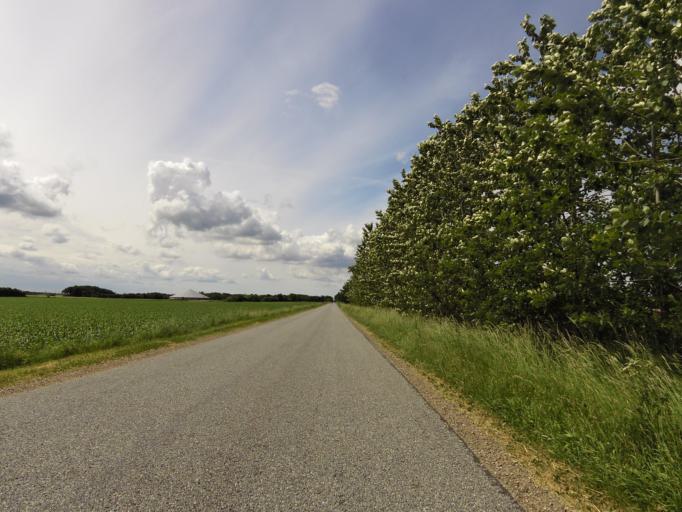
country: DK
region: South Denmark
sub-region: Esbjerg Kommune
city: Ribe
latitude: 55.2626
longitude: 8.8678
